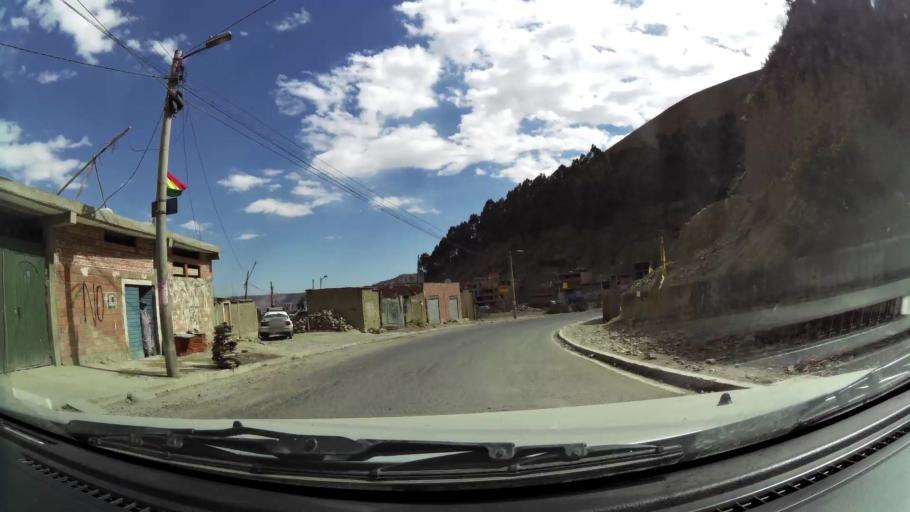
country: BO
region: La Paz
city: La Paz
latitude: -16.4618
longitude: -68.1078
